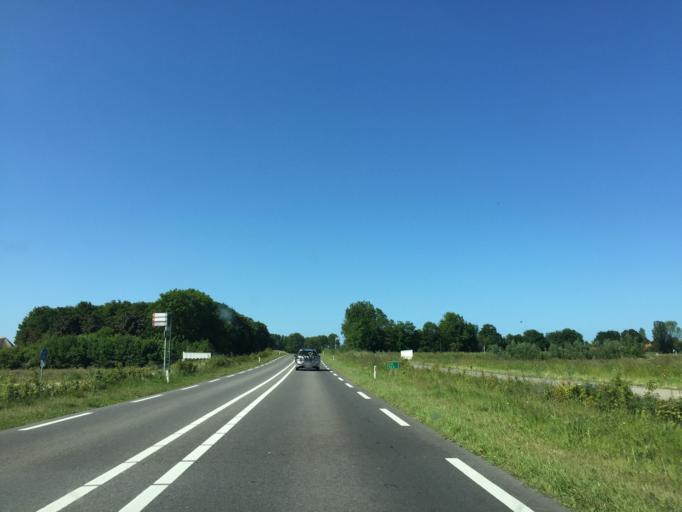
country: NL
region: Zeeland
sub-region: Schouwen-Duiveland
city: Haamstede
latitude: 51.6899
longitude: 3.7423
